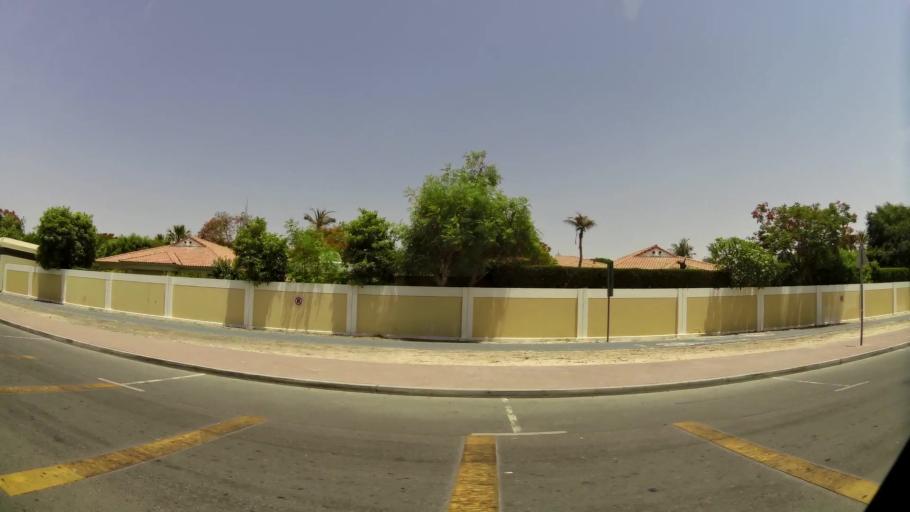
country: AE
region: Dubai
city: Dubai
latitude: 25.2000
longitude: 55.2421
